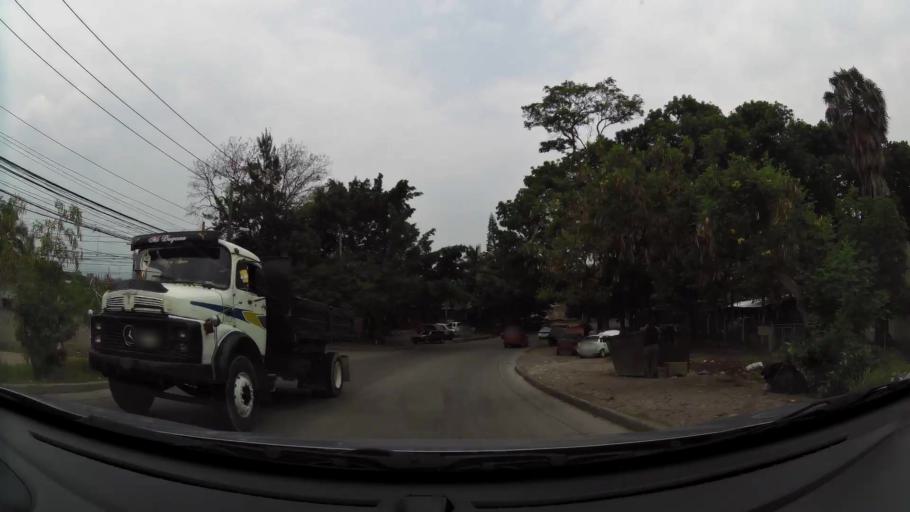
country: HN
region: Francisco Morazan
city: Tegucigalpa
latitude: 14.0641
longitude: -87.2013
